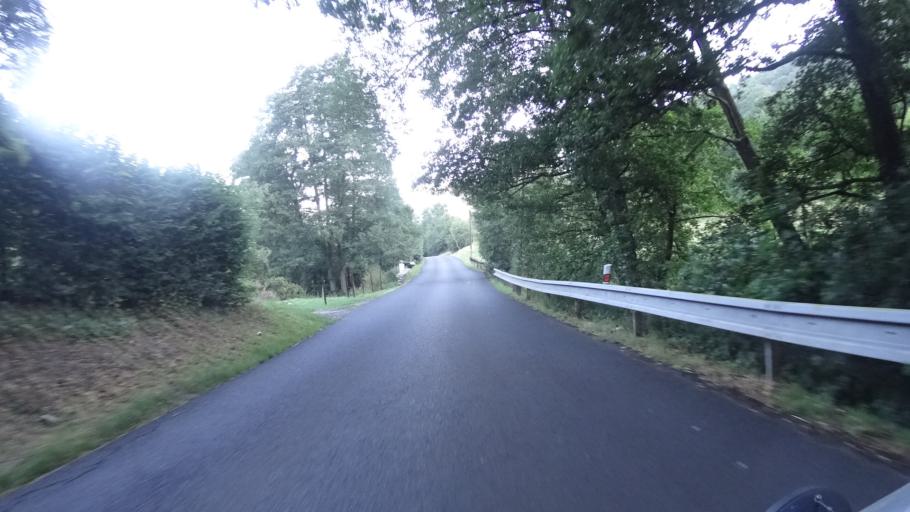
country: CZ
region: Ustecky
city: Lovosice
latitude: 50.5878
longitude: 14.0768
